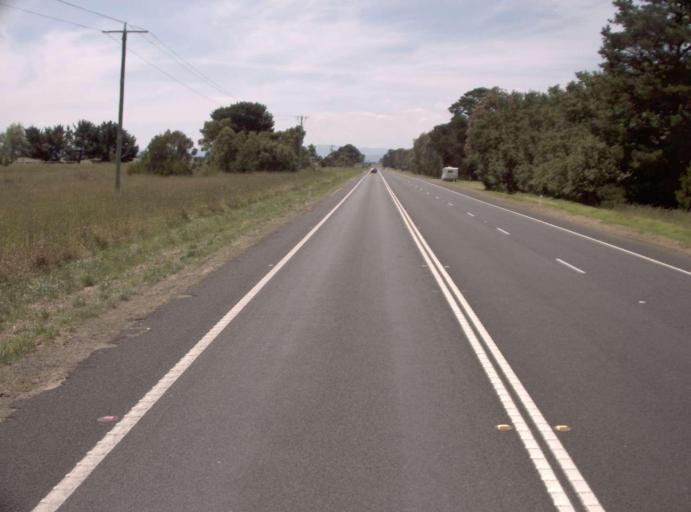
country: AU
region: Victoria
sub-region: Wellington
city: Sale
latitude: -38.0462
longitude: 147.0640
